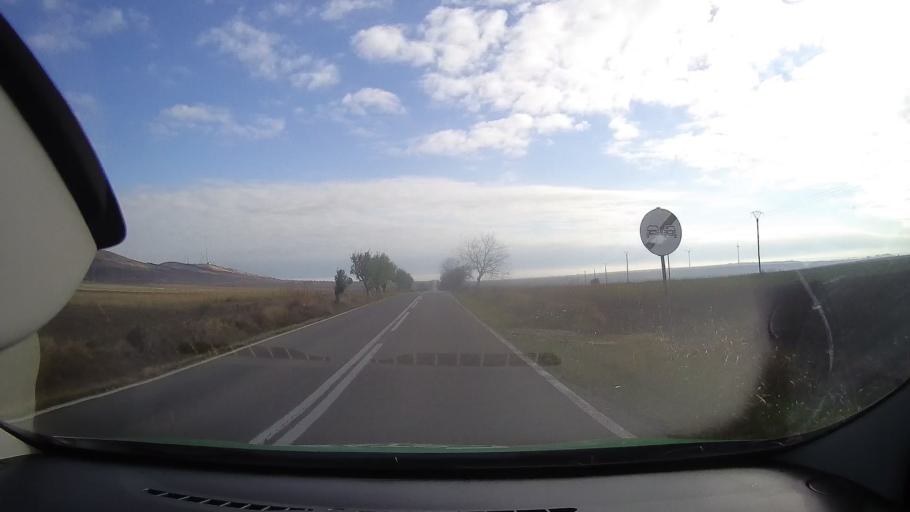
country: RO
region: Tulcea
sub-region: Comuna Bestepe
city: Bestepe
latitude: 45.0780
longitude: 29.0441
